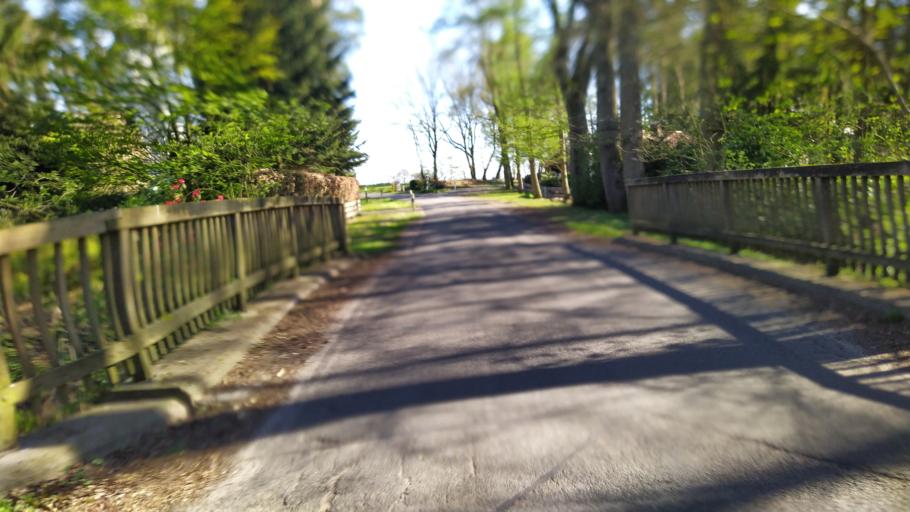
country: DE
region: Lower Saxony
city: Heeslingen
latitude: 53.3303
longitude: 9.3821
